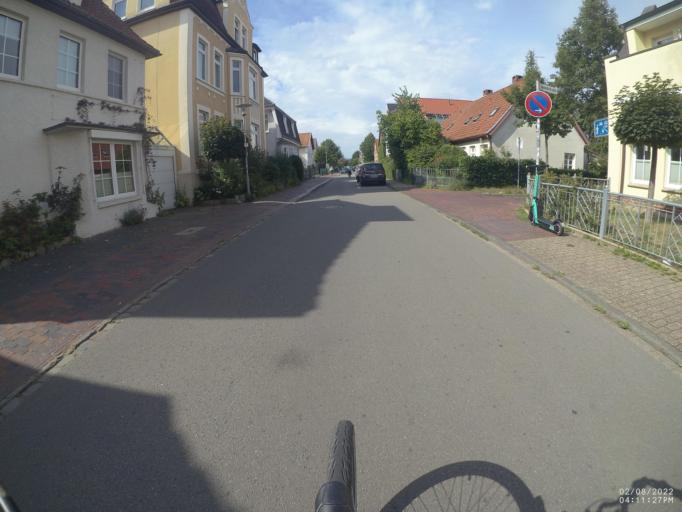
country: DE
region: Lower Saxony
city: Oldenburg
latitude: 53.1472
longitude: 8.2097
